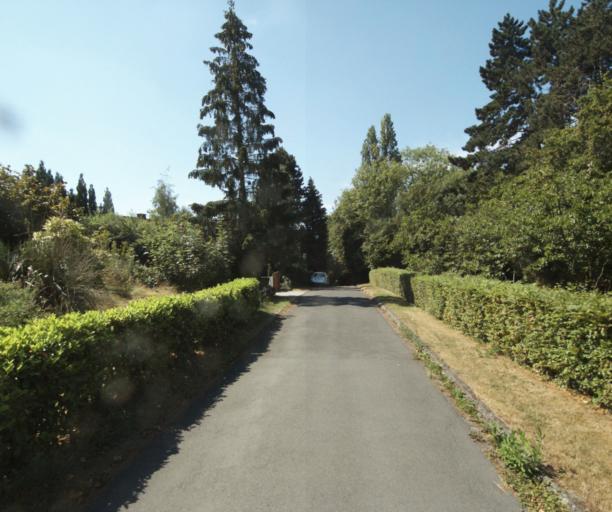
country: FR
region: Nord-Pas-de-Calais
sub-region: Departement du Nord
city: Neuville-en-Ferrain
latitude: 50.7639
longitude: 3.1439
